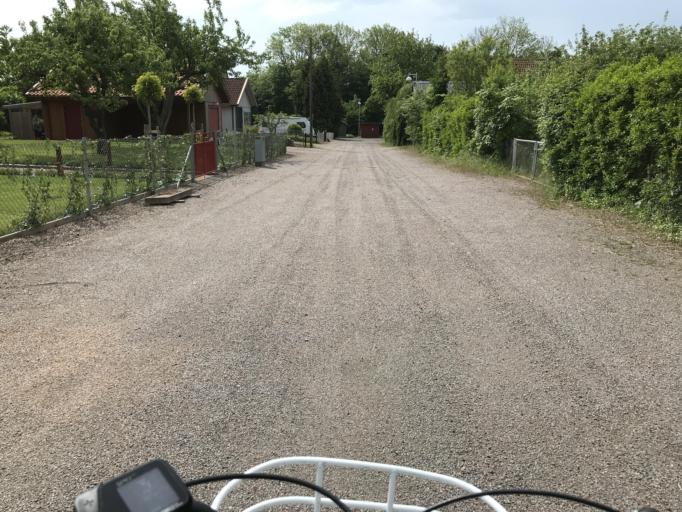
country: SE
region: Skane
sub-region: Landskrona
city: Landskrona
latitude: 55.9009
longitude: 12.8329
